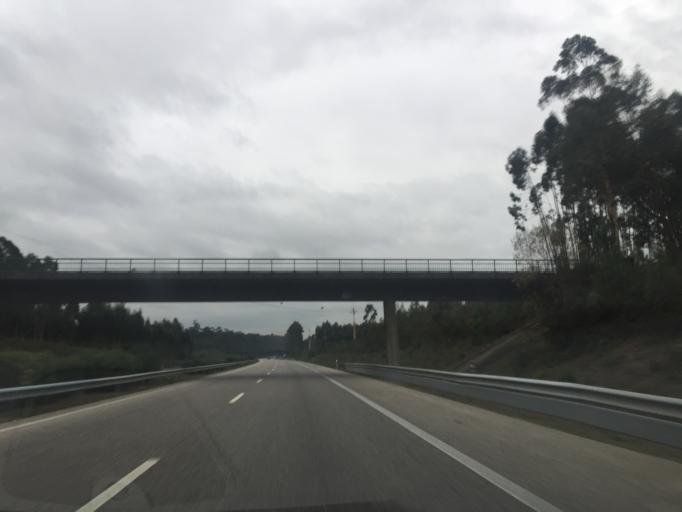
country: PT
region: Leiria
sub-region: Pombal
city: Pombal
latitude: 39.8709
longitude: -8.7037
